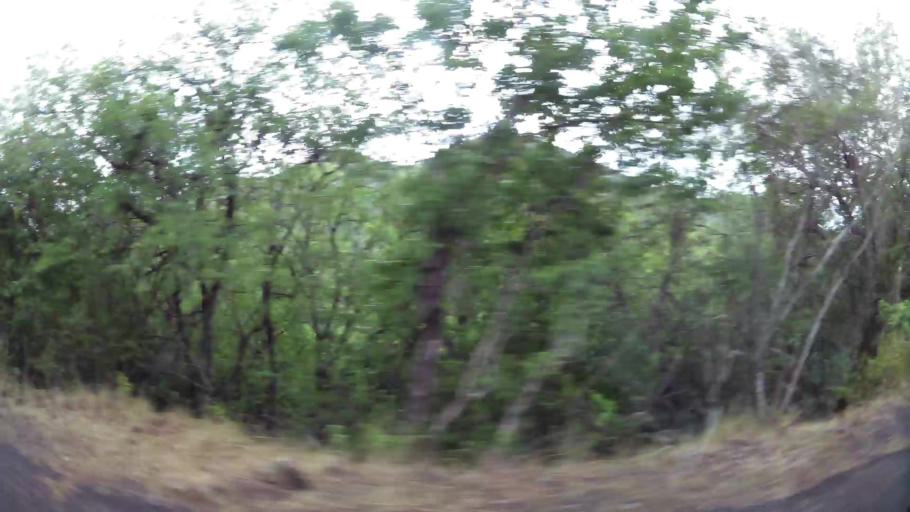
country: KN
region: Saint James Windwa
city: Newcastle
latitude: 17.1983
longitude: -62.5964
